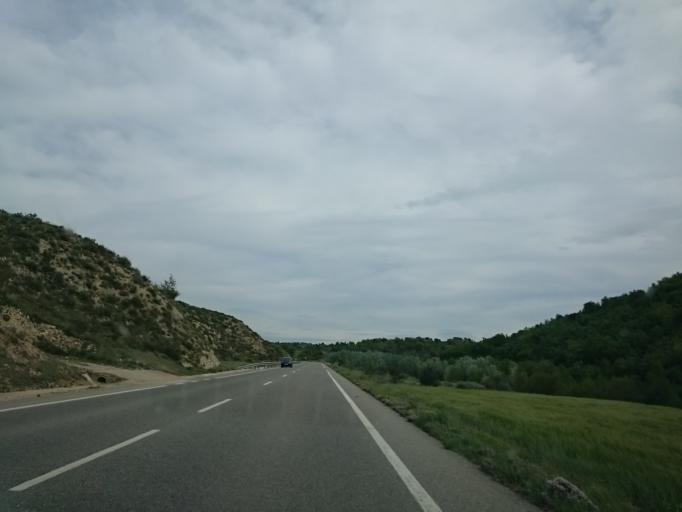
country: ES
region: Catalonia
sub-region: Provincia de Lleida
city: Tora de Riubregos
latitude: 41.8282
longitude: 1.3379
